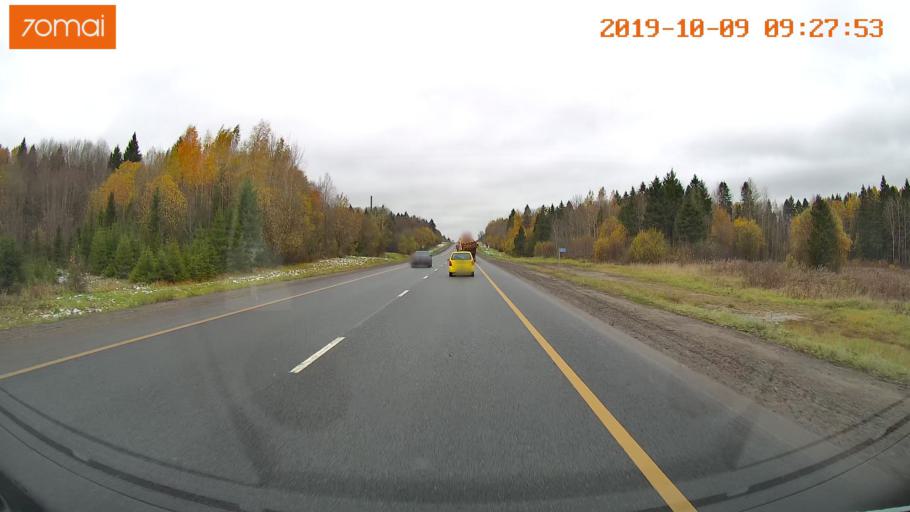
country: RU
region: Vologda
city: Vologda
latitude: 59.1176
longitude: 39.9734
